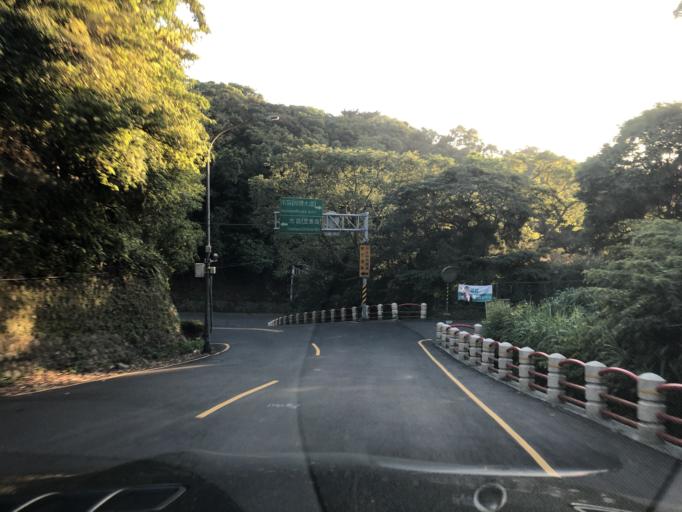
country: TW
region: Taipei
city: Taipei
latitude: 25.1427
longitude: 121.5566
